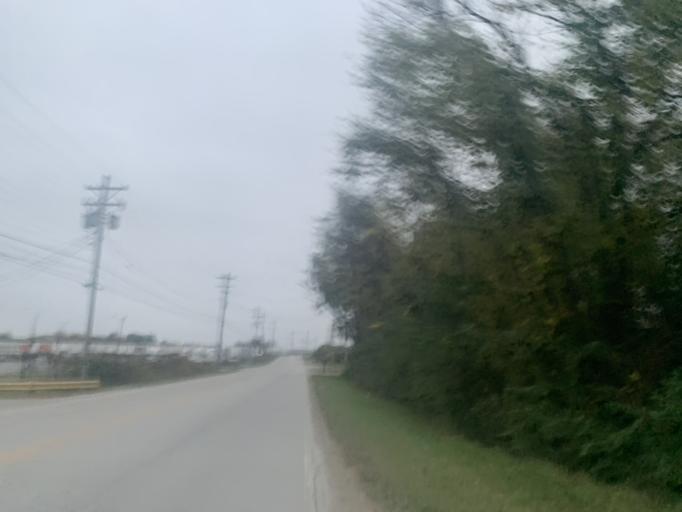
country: US
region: Kentucky
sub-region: Jefferson County
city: Shively
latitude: 38.2160
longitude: -85.8138
